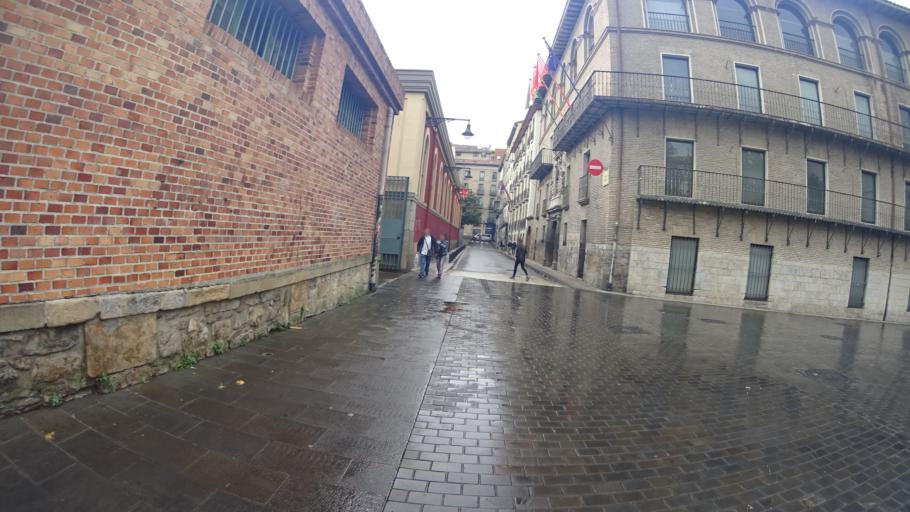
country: ES
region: Navarre
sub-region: Provincia de Navarra
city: Pamplona
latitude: 42.8195
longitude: -1.6443
